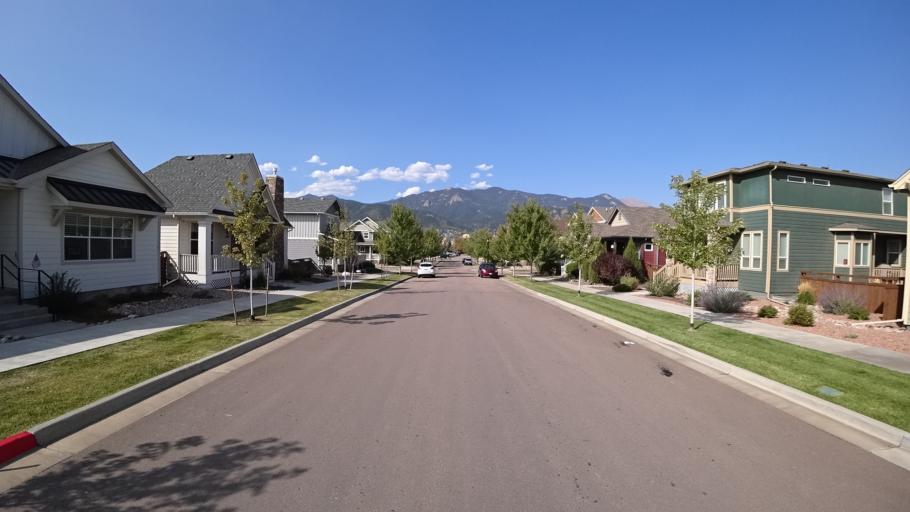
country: US
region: Colorado
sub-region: El Paso County
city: Colorado Springs
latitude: 38.8315
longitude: -104.8515
